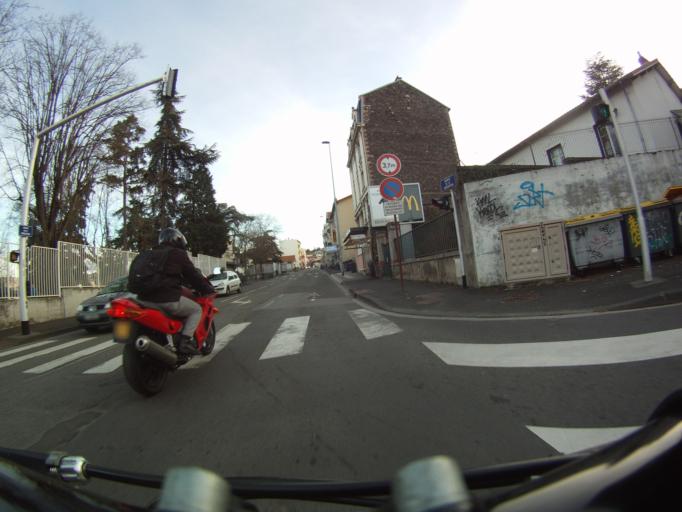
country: FR
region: Auvergne
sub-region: Departement du Puy-de-Dome
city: Beaumont
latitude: 45.7616
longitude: 3.0823
